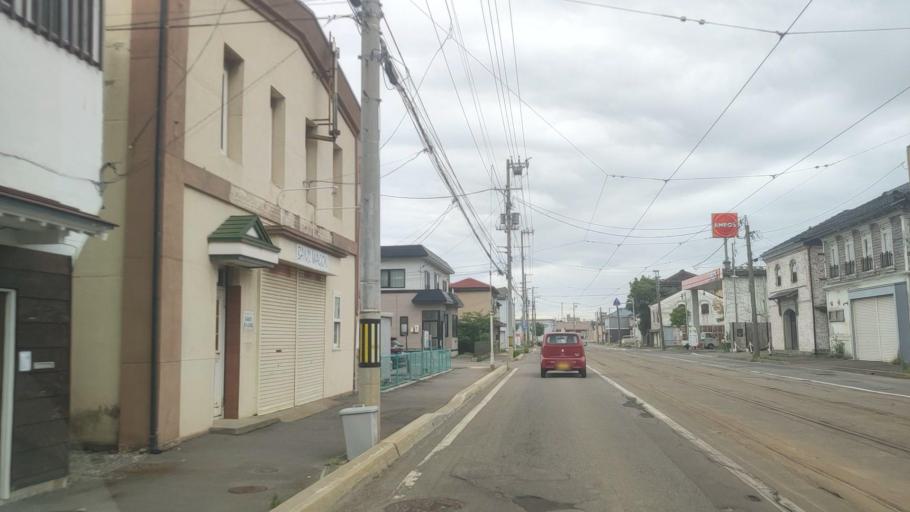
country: JP
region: Hokkaido
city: Hakodate
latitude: 41.7710
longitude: 140.7077
